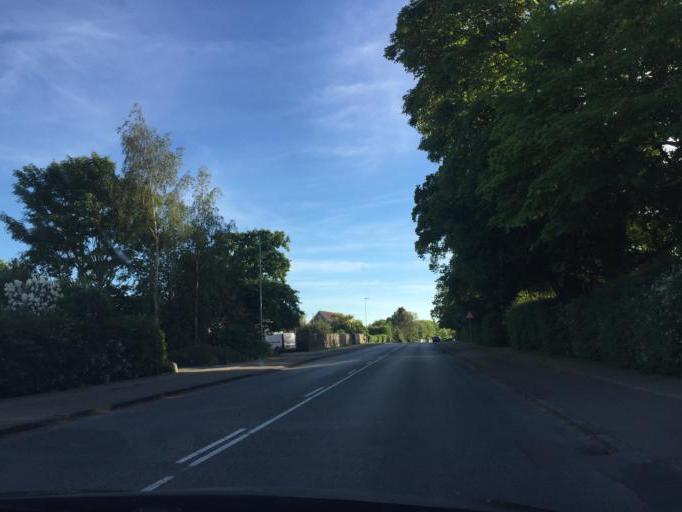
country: DK
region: Zealand
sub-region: Slagelse Kommune
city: Slagelse
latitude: 55.3916
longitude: 11.3298
